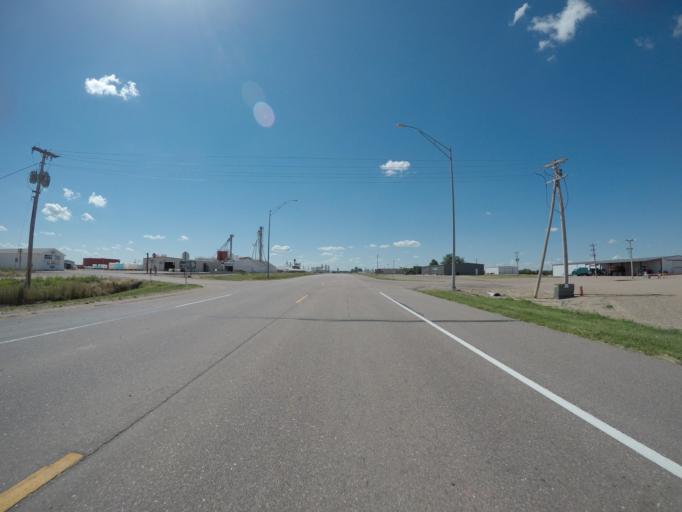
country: US
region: Nebraska
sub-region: Chase County
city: Imperial
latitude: 40.5049
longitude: -101.6228
